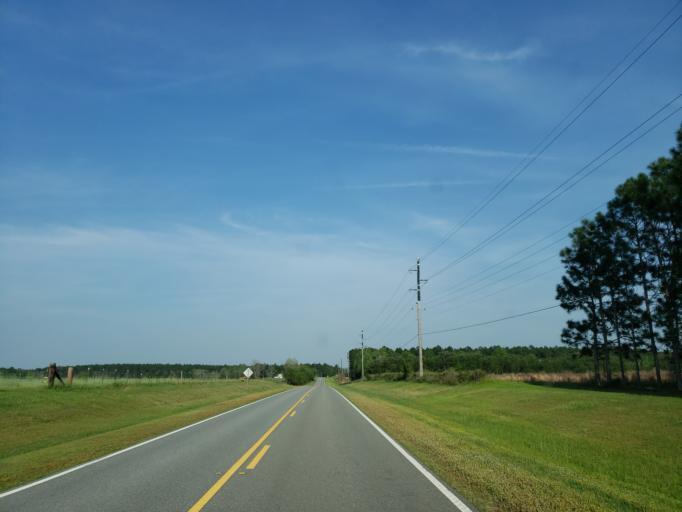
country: US
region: Georgia
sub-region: Tift County
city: Tifton
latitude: 31.5724
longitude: -83.5214
